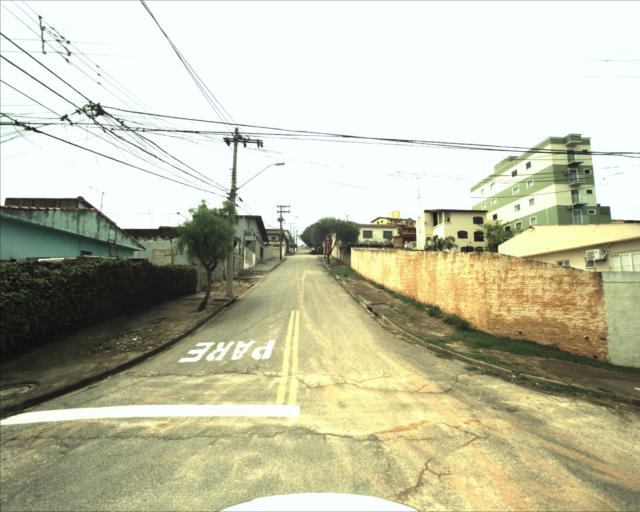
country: BR
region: Sao Paulo
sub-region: Sorocaba
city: Sorocaba
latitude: -23.5078
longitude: -47.4967
